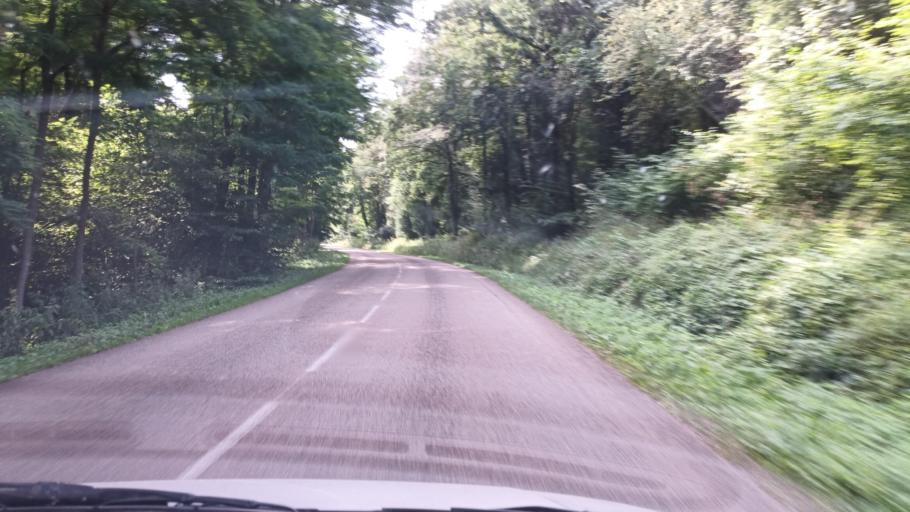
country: FR
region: Bourgogne
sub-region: Departement de l'Yonne
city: Villeneuve-sur-Yonne
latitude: 48.0745
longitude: 3.2677
